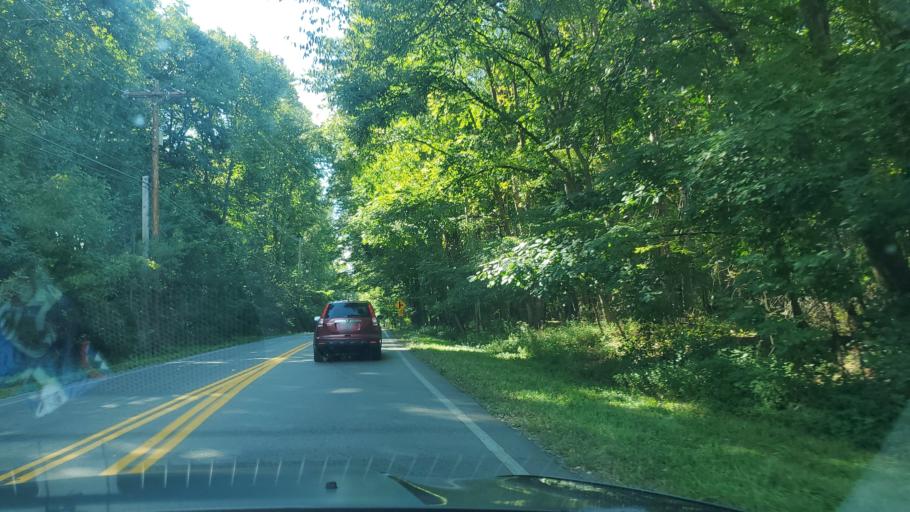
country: US
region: Ohio
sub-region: Mahoning County
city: Boardman
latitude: 41.0466
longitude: -80.6842
